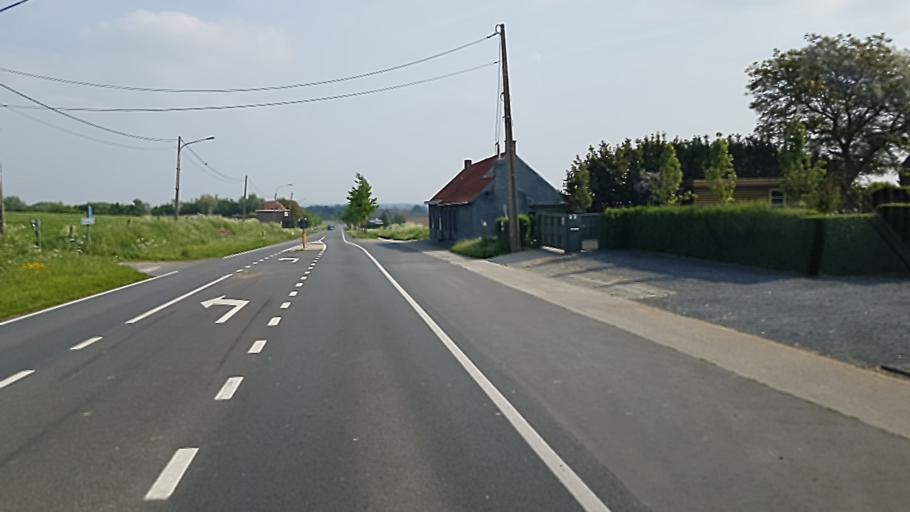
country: BE
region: Flanders
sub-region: Provincie West-Vlaanderen
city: Zwevegem
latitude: 50.7566
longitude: 3.3123
